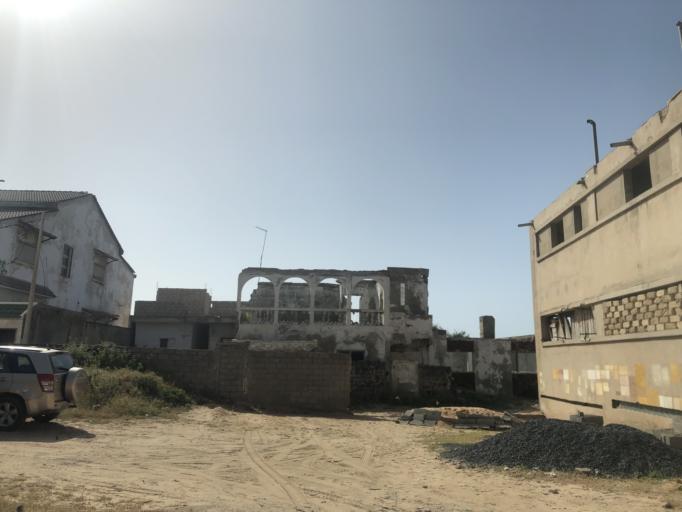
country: SN
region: Dakar
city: Mermoz Boabab
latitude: 14.7580
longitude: -17.4876
